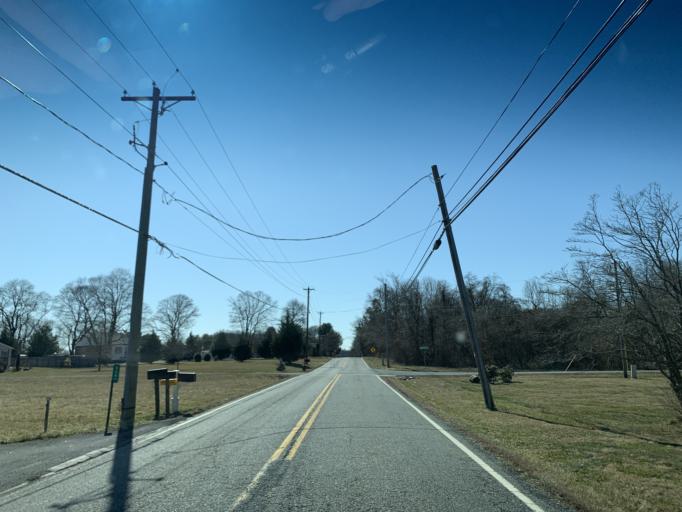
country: US
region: Maryland
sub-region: Cecil County
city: Rising Sun
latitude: 39.6302
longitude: -76.0771
